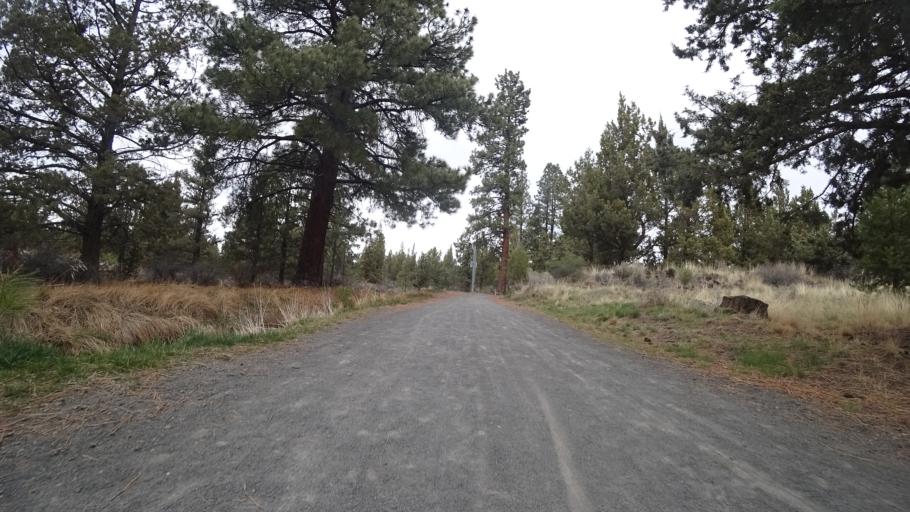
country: US
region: Oregon
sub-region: Deschutes County
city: Bend
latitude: 44.0415
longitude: -121.2789
